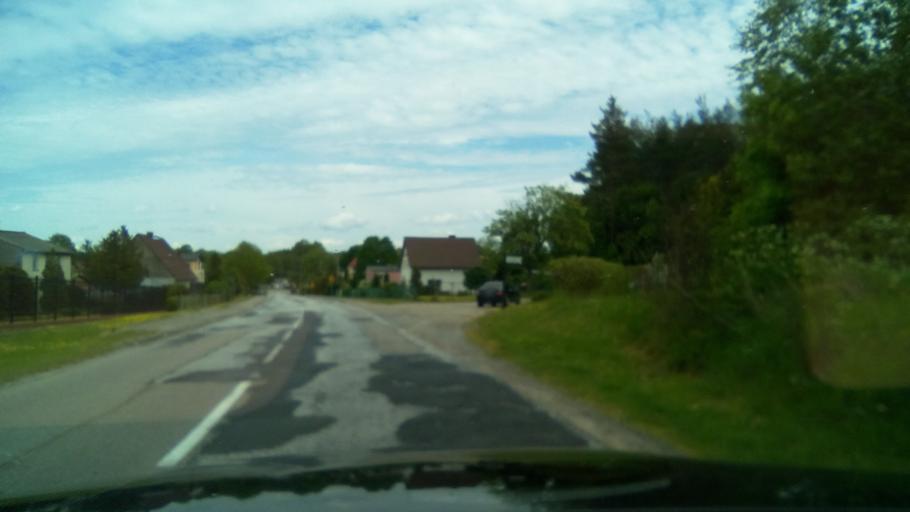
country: PL
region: Pomeranian Voivodeship
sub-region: Powiat bytowski
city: Czarna Dabrowka
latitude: 54.3133
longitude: 17.4864
